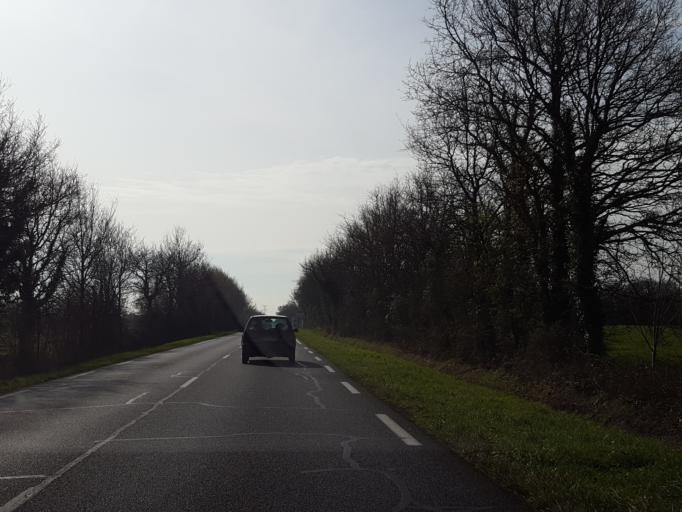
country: FR
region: Pays de la Loire
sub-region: Departement de la Vendee
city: Saligny
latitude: 46.8088
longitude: -1.4577
